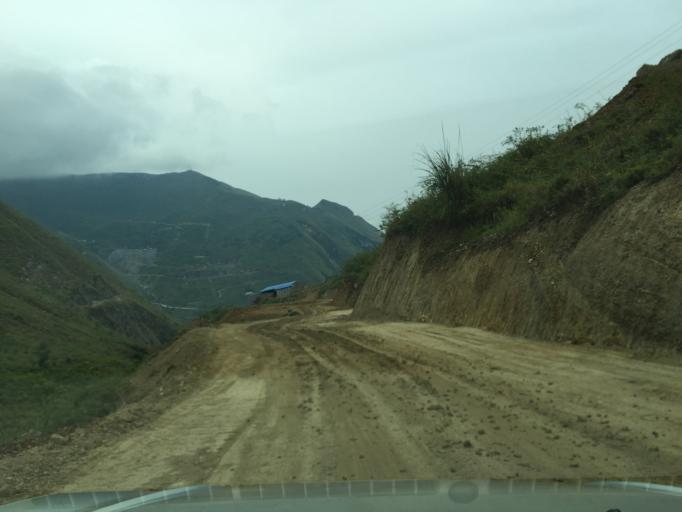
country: CN
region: Guizhou Sheng
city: Liupanshui
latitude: 25.9645
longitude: 105.2386
